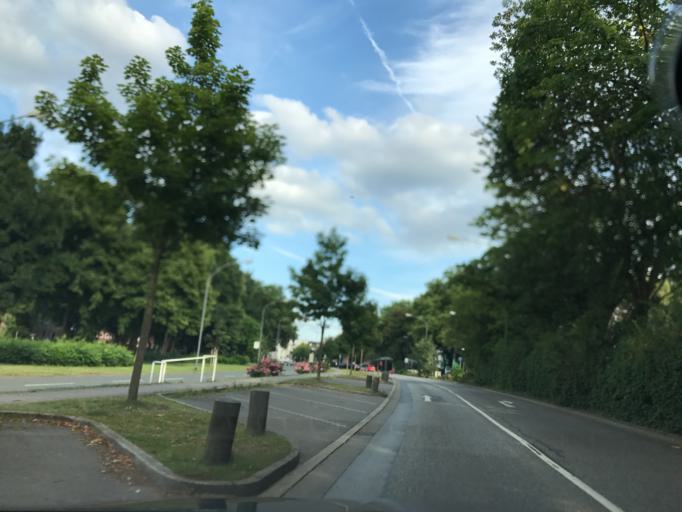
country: DE
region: North Rhine-Westphalia
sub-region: Regierungsbezirk Dusseldorf
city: Essen
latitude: 51.4354
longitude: 6.9989
